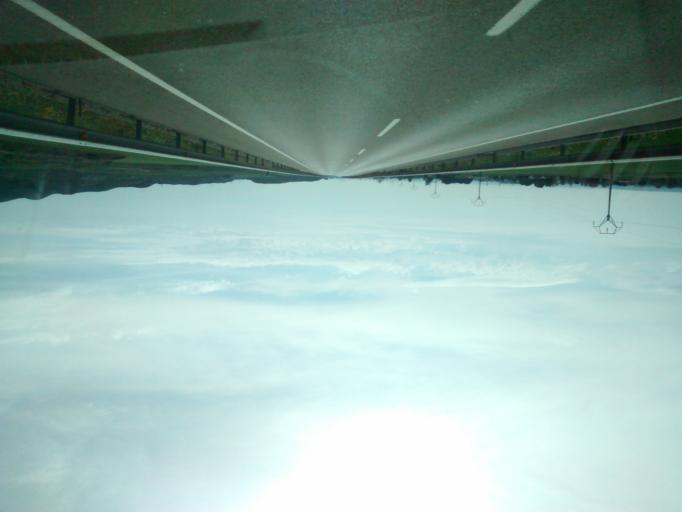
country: ES
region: Aragon
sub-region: Provincia de Zaragoza
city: El Burgo de Ebro
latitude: 41.5559
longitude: -0.7204
